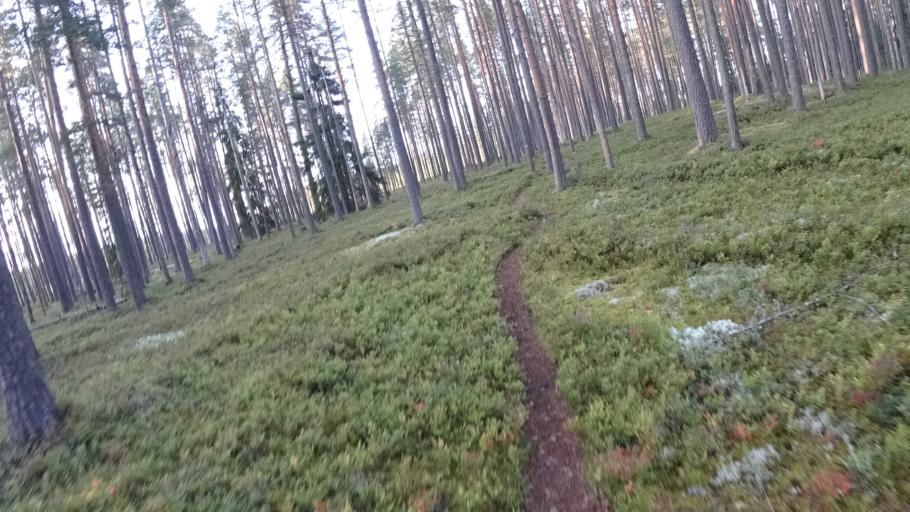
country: FI
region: North Karelia
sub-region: Joensuu
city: Ilomantsi
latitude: 62.5842
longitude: 31.1859
